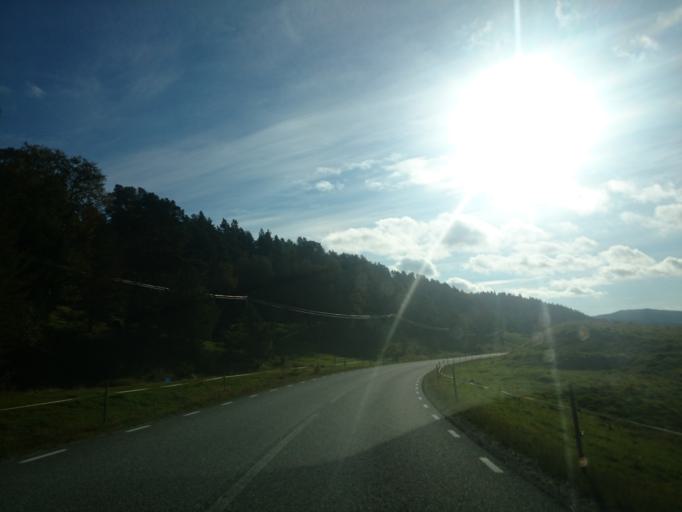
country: NO
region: Sor-Trondelag
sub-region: Tydal
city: Aas
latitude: 62.6217
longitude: 12.4678
